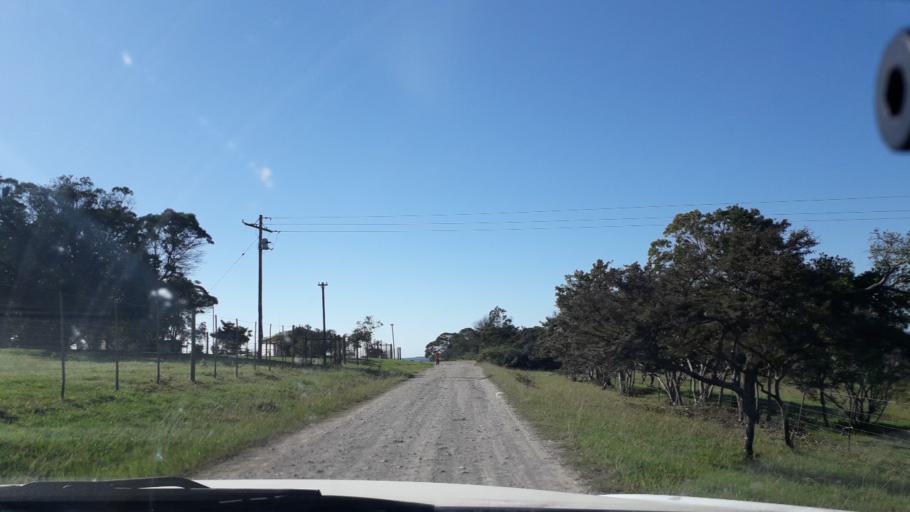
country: ZA
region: Eastern Cape
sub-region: Buffalo City Metropolitan Municipality
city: East London
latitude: -32.8414
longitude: 27.9752
